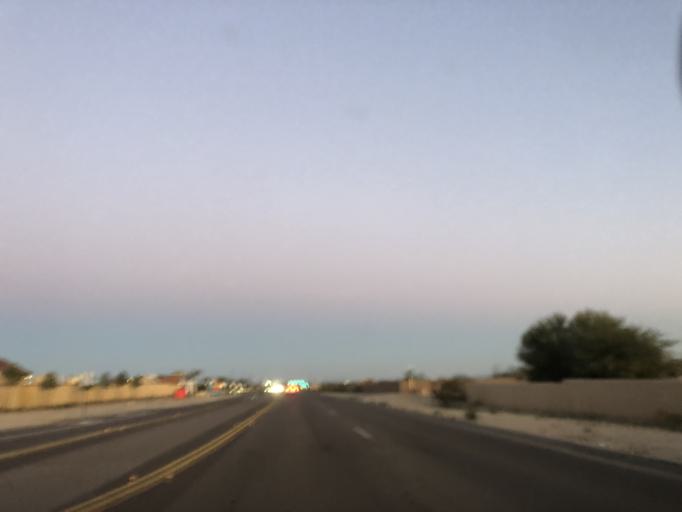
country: US
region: Arizona
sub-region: Maricopa County
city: Citrus Park
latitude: 33.4937
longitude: -112.4856
